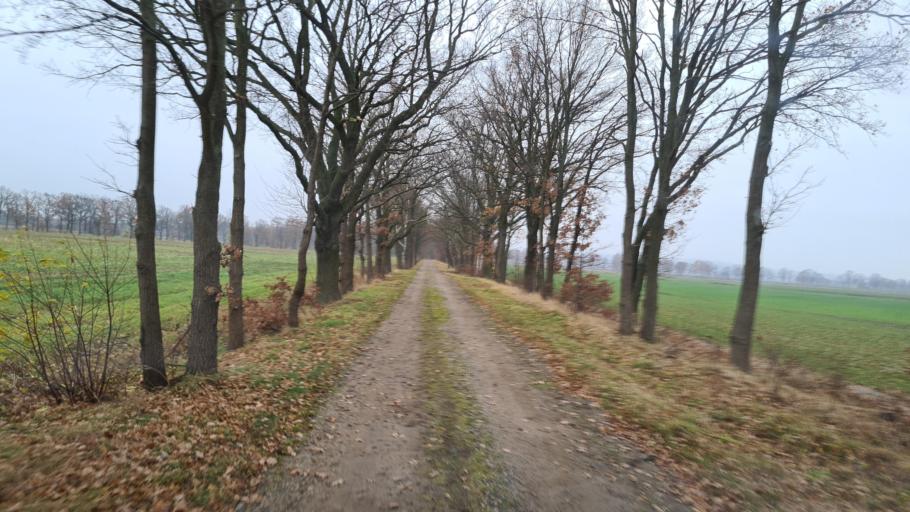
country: DE
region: Brandenburg
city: Schraden
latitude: 51.4105
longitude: 13.7061
